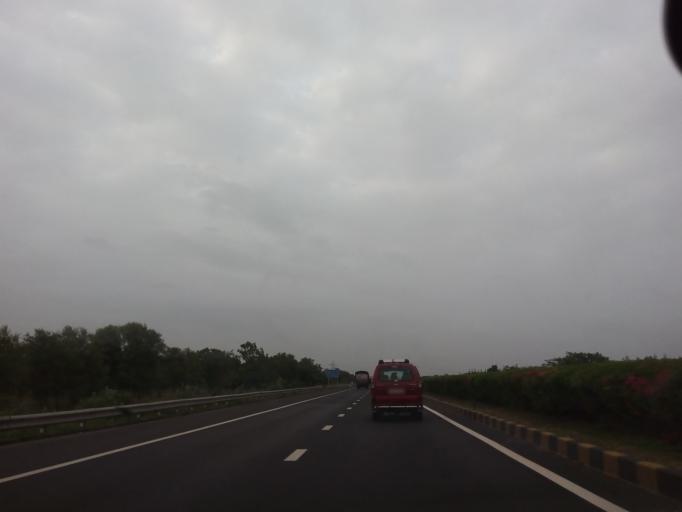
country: IN
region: Gujarat
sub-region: Kheda
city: Nadiad
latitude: 22.7688
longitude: 72.8516
